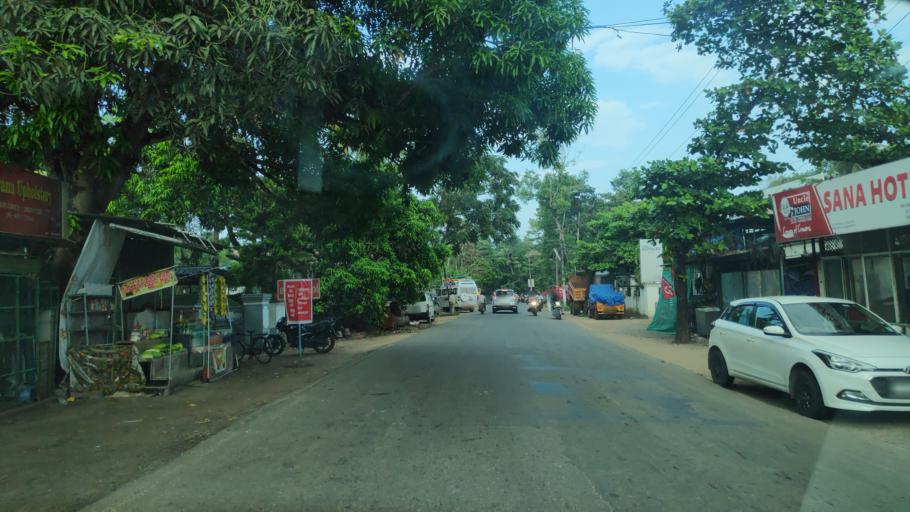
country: IN
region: Kerala
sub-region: Alappuzha
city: Alleppey
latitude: 9.5652
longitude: 76.3466
